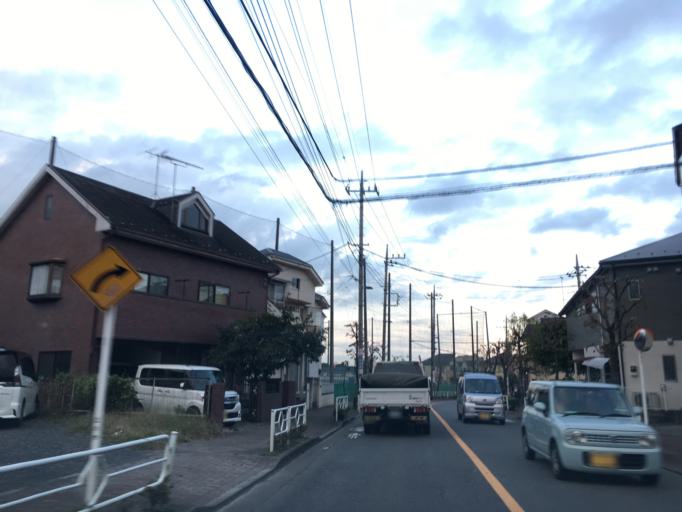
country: JP
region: Tokyo
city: Hino
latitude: 35.7265
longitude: 139.4106
